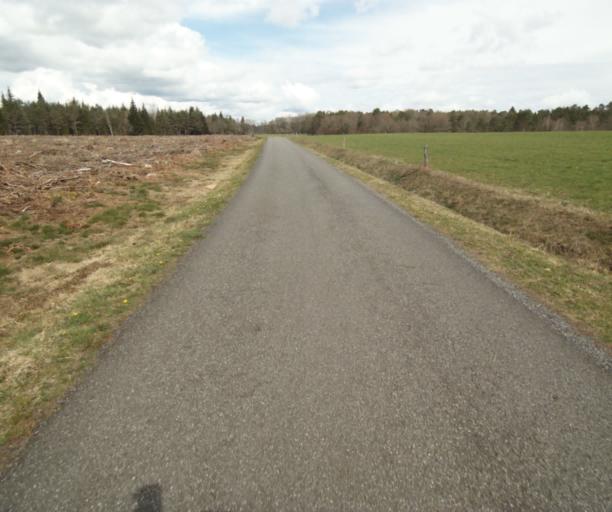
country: FR
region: Limousin
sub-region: Departement de la Correze
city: Correze
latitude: 45.3528
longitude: 1.9561
